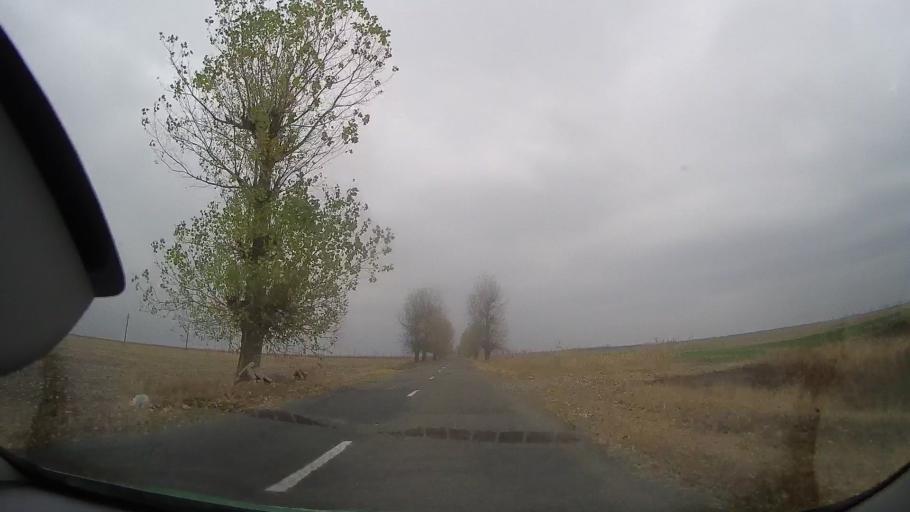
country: RO
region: Ialomita
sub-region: Comuna Grindu
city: Grindu
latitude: 44.7981
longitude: 26.8843
